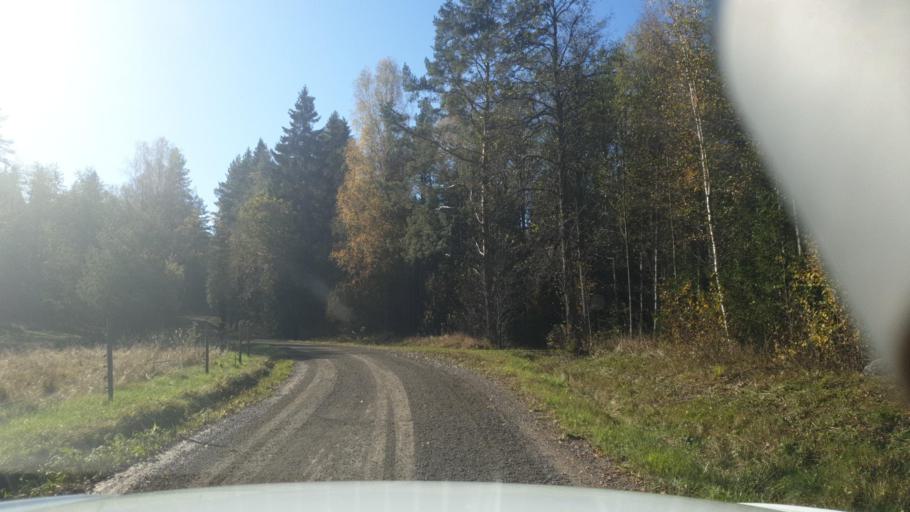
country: SE
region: Vaermland
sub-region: Grums Kommun
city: Grums
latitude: 59.5039
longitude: 12.9267
